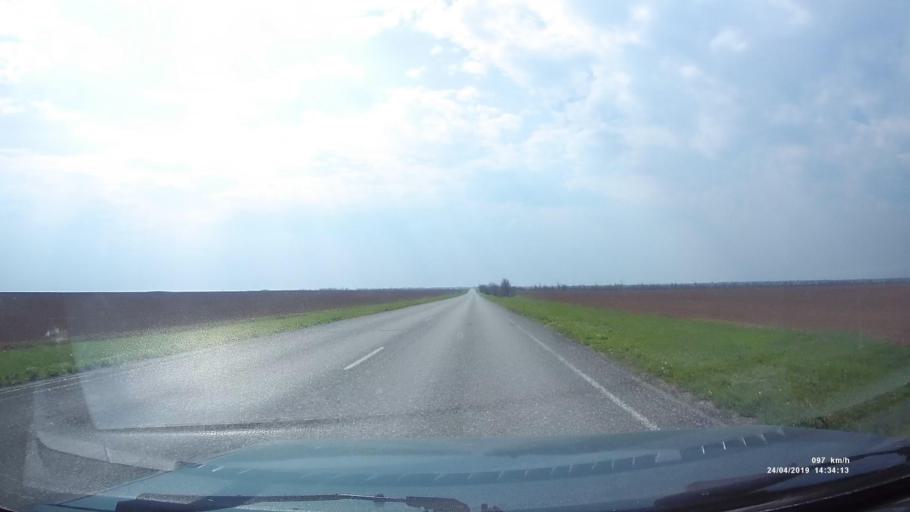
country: RU
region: Kalmykiya
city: Arshan'
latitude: 46.3737
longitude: 43.9364
